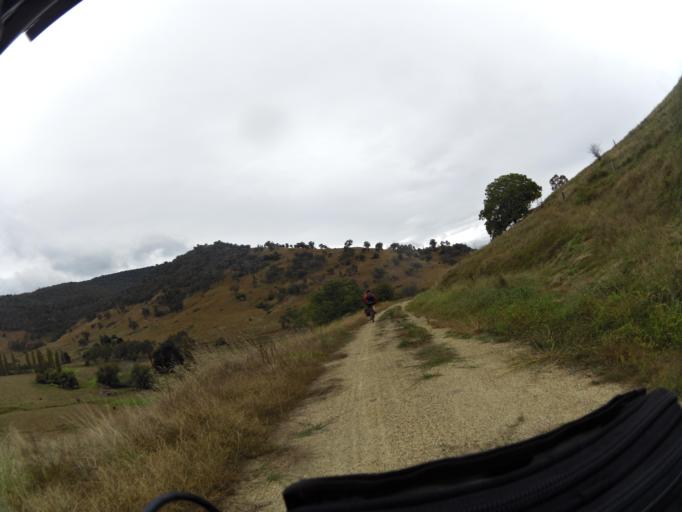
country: AU
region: New South Wales
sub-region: Albury Municipality
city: East Albury
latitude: -36.1853
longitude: 147.3582
